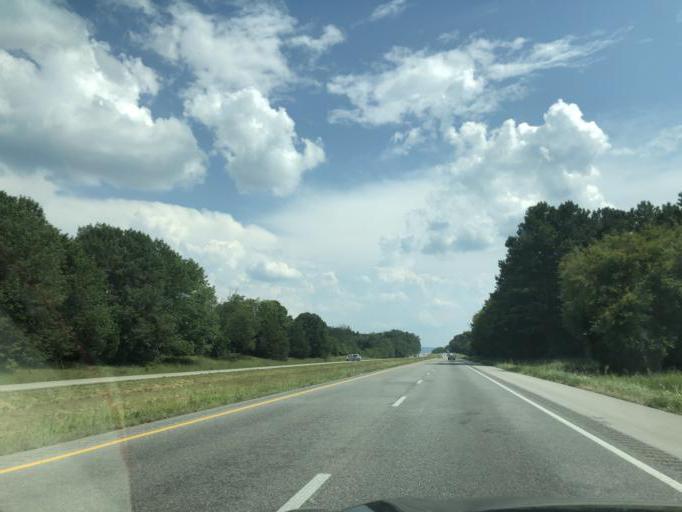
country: US
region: Tennessee
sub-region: Franklin County
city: Sewanee
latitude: 35.3429
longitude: -85.9425
